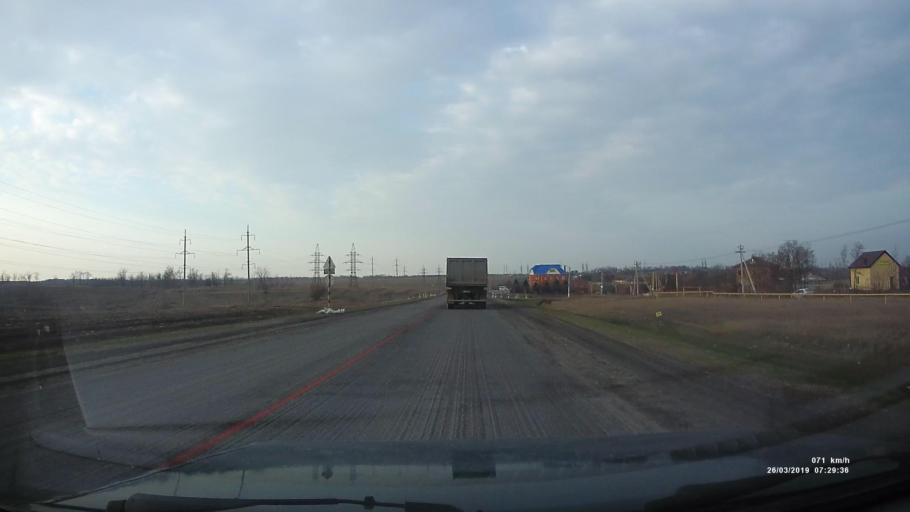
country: RU
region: Rostov
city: Novobessergenovka
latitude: 47.2437
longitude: 38.8154
